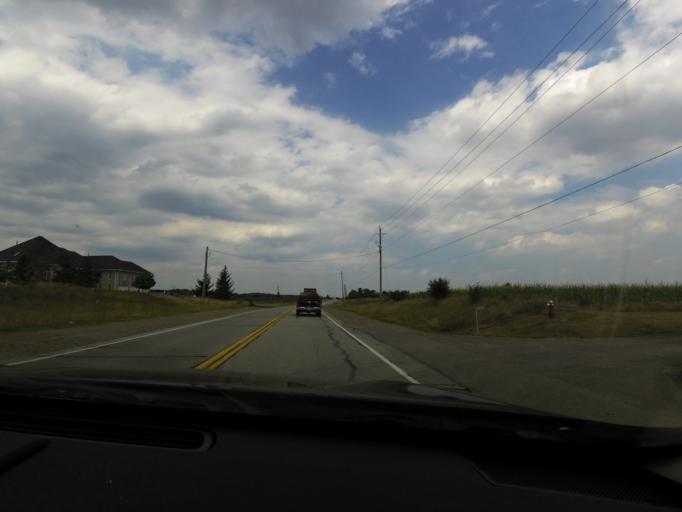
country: CA
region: Ontario
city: Brampton
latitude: 43.7783
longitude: -79.8731
